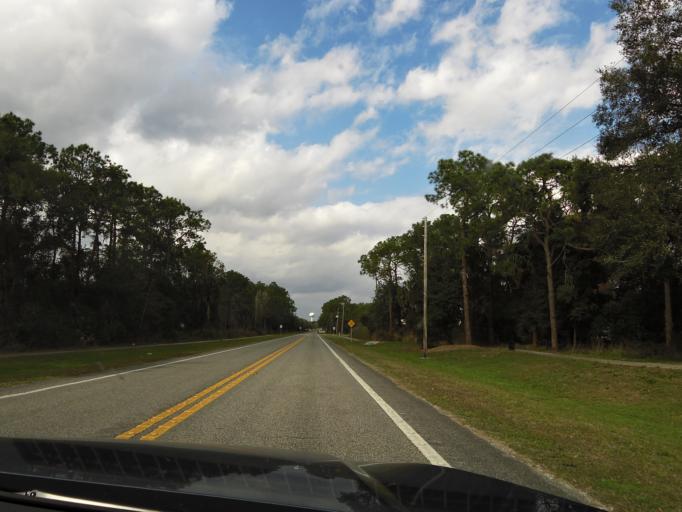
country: US
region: Florida
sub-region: Volusia County
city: Pierson
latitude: 29.2257
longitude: -81.4611
